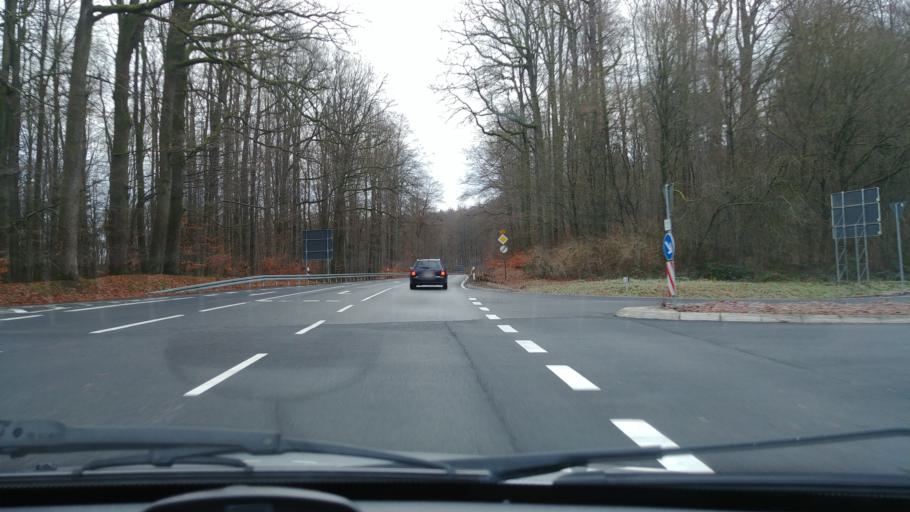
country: DE
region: Bavaria
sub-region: Regierungsbezirk Unterfranken
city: Rothenbuch
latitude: 49.9956
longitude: 9.3762
